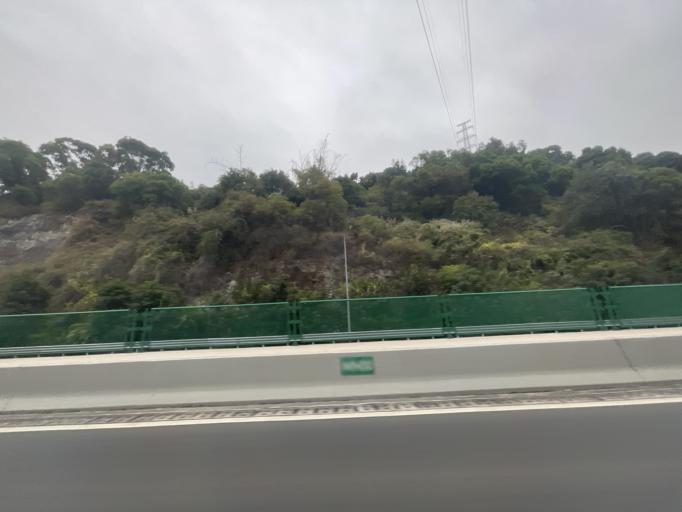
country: CN
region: Guangdong
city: Nansha
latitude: 22.7665
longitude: 113.5593
